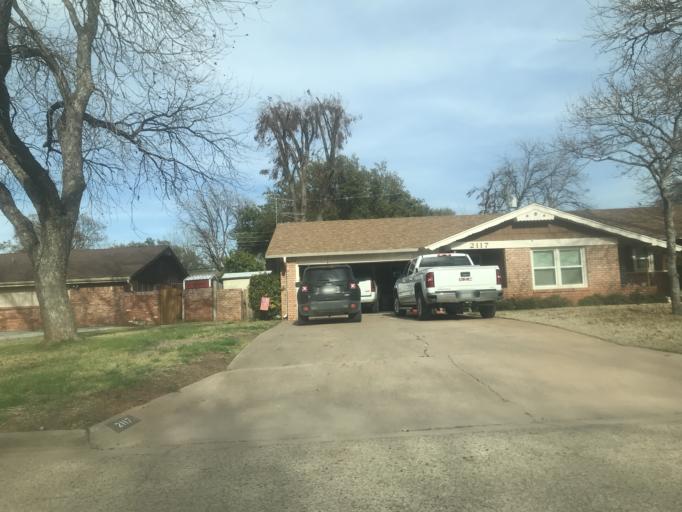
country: US
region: Texas
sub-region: Taylor County
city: Abilene
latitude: 32.4230
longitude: -99.7721
